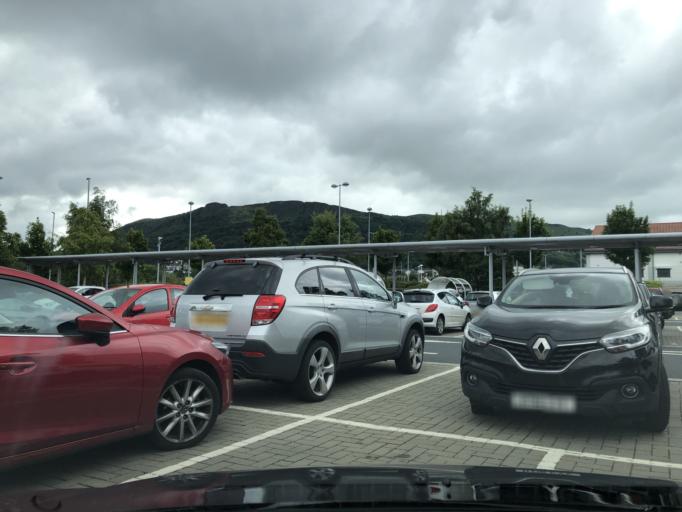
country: GB
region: Northern Ireland
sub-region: Newtownabbey District
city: Newtownabbey
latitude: 54.6576
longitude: -5.9207
